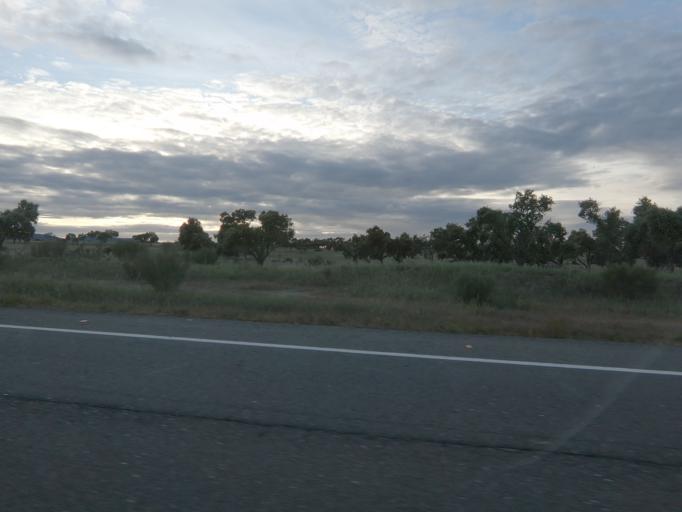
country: ES
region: Extremadura
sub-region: Provincia de Caceres
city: Malpartida de Caceres
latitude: 39.3641
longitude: -6.4611
